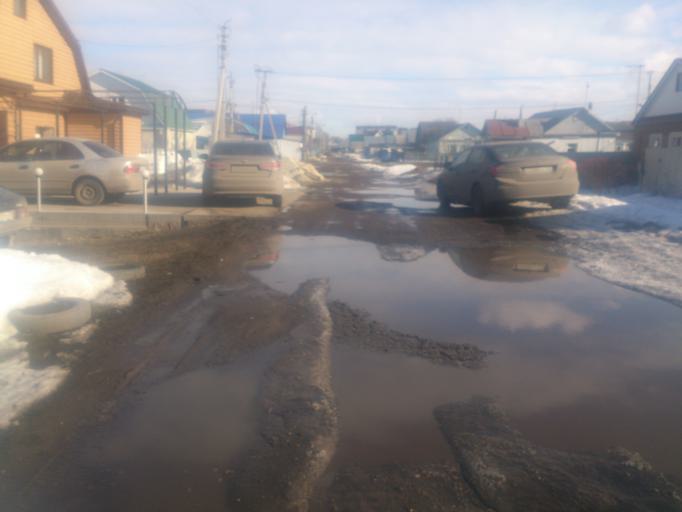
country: RU
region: Ulyanovsk
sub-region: Ulyanovskiy Rayon
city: Ulyanovsk
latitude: 54.2674
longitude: 48.2881
